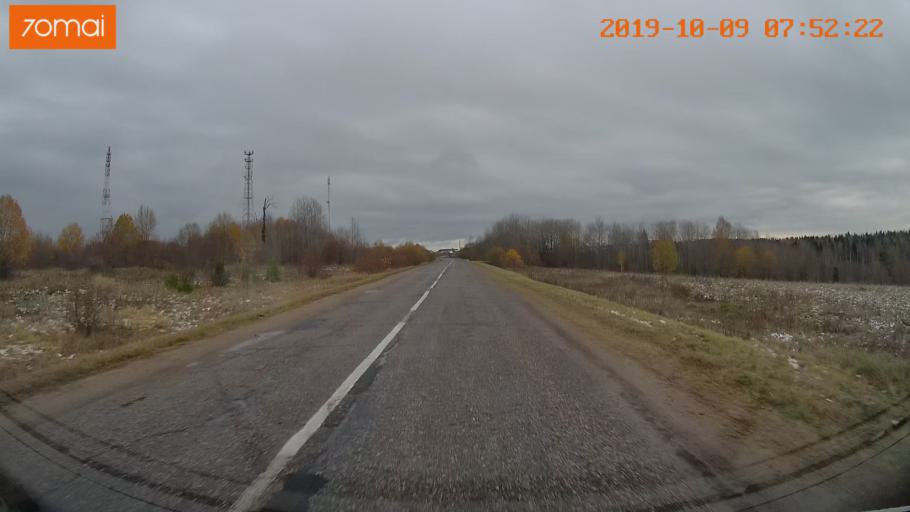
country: RU
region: Jaroslavl
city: Kukoboy
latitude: 58.6904
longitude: 39.8864
